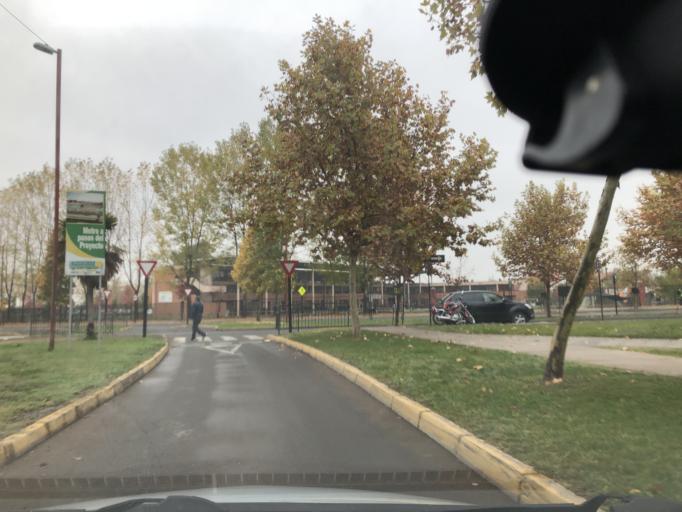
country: CL
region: Santiago Metropolitan
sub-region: Provincia de Cordillera
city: Puente Alto
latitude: -33.5956
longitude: -70.5804
